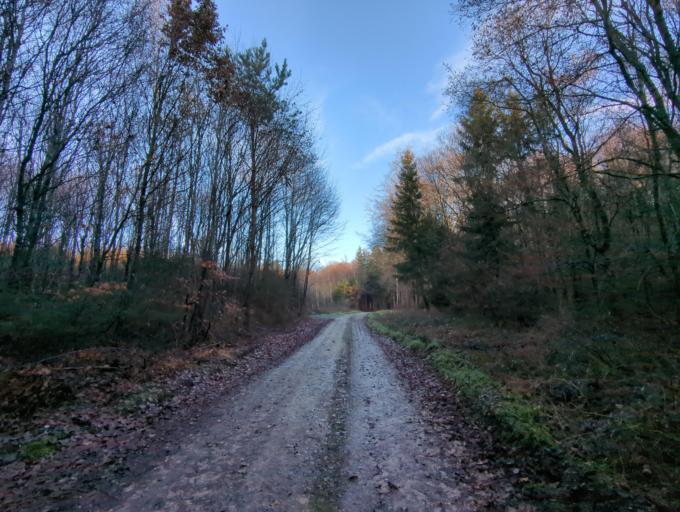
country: DE
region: Bavaria
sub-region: Swabia
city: Wasserburg
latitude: 48.4289
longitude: 10.3103
